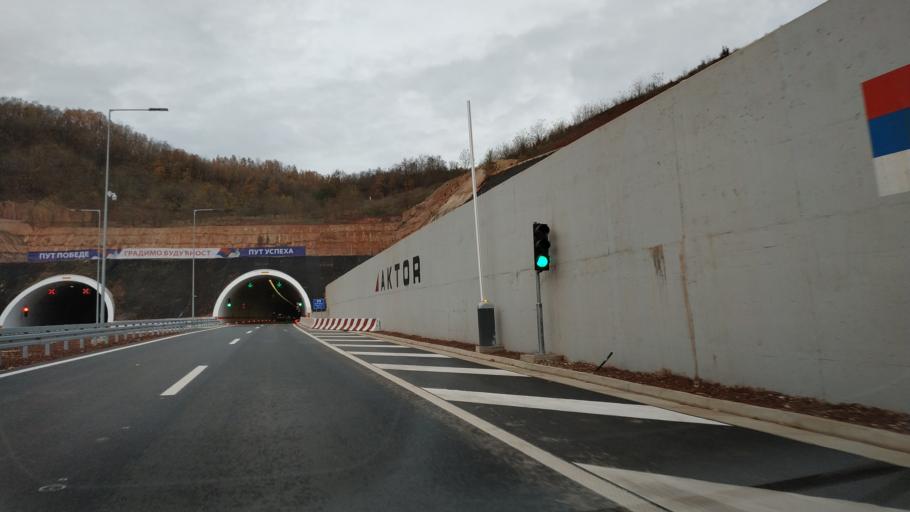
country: RS
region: Central Serbia
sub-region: Nisavski Okrug
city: Gadzin Han
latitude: 43.2679
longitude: 22.1415
